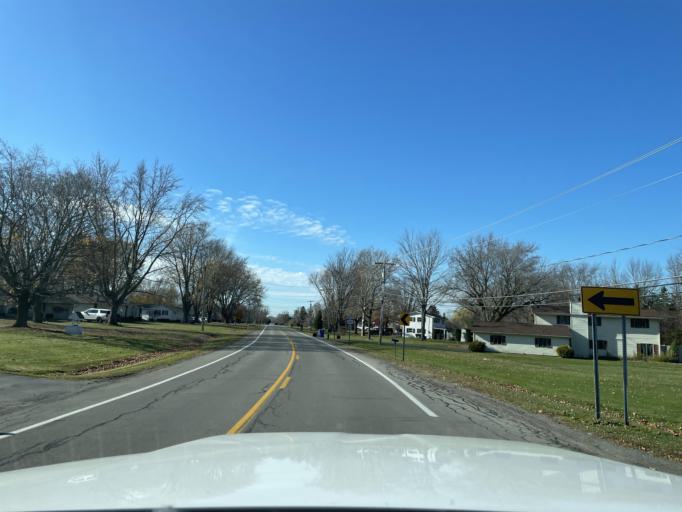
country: US
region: New York
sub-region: Orleans County
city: Medina
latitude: 43.2200
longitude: -78.4206
